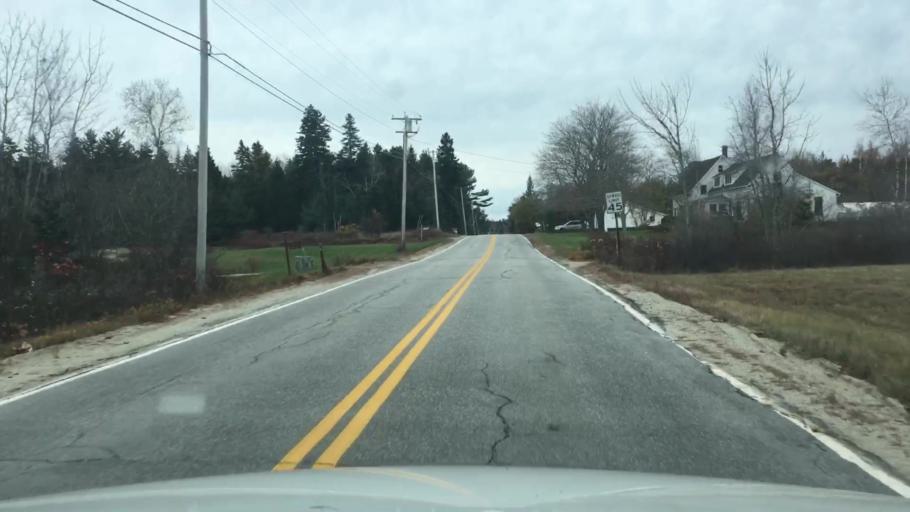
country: US
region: Maine
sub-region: Hancock County
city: Sedgwick
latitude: 44.3437
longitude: -68.5580
